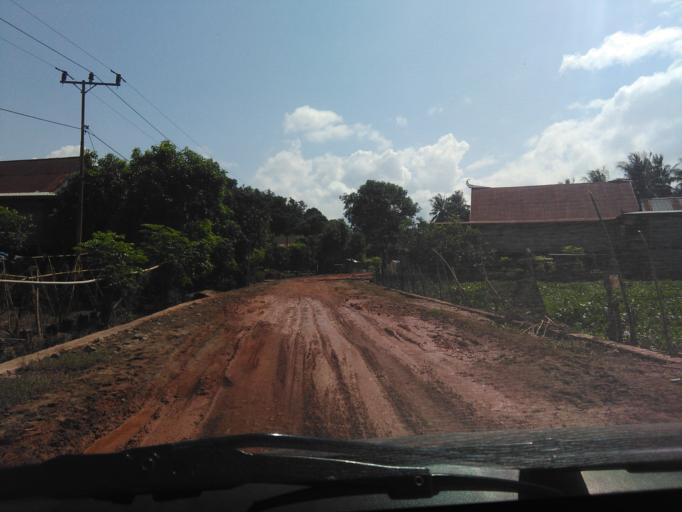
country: ID
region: South Sulawesi
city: Tancung
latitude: -4.0169
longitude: 119.9248
